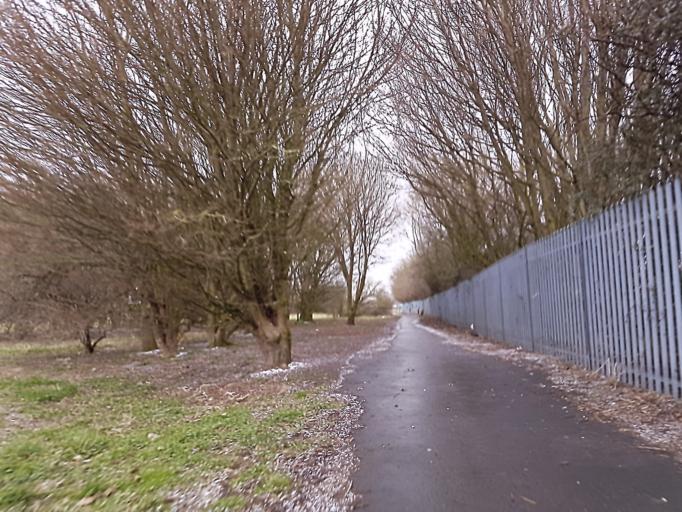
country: GB
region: England
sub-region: North East Lincolnshire
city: Great Coates
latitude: 53.5654
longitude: -0.1194
